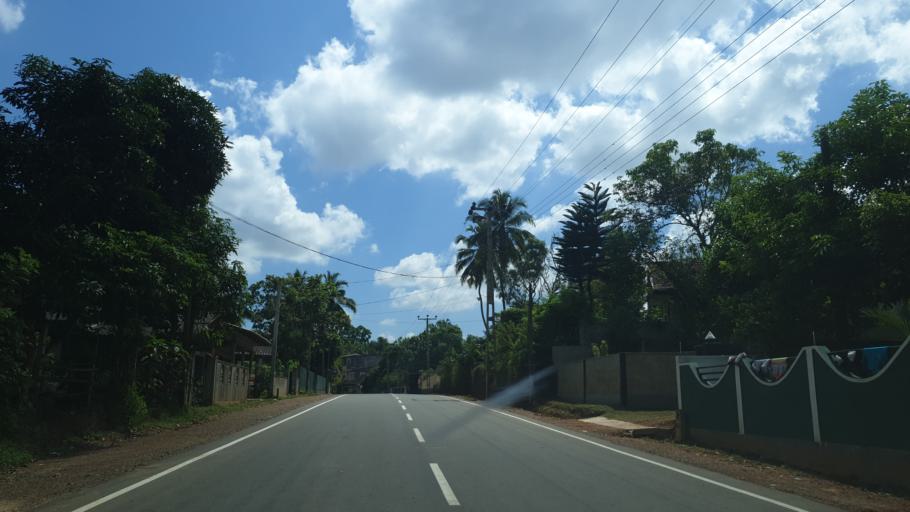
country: LK
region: Western
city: Panadura
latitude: 6.6647
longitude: 79.9688
